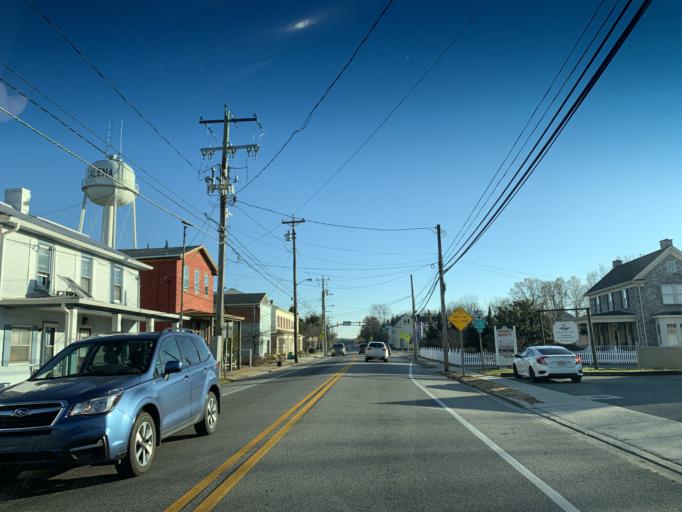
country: US
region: Delaware
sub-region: New Castle County
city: Townsend
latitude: 39.3418
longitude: -75.8790
